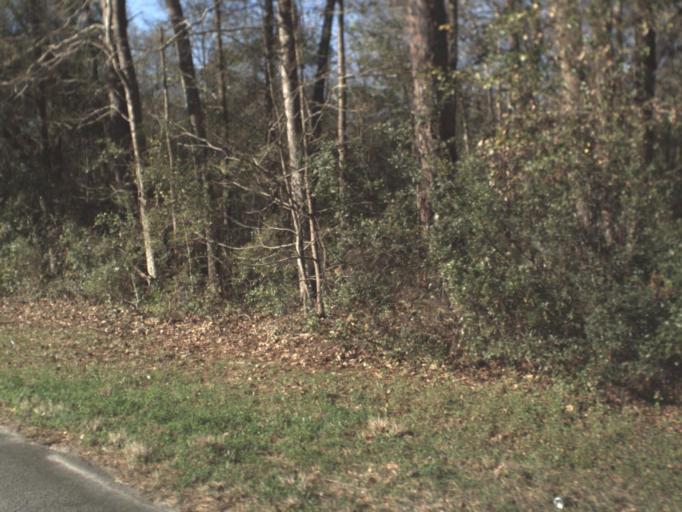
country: US
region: Georgia
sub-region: Brooks County
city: Quitman
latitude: 30.5786
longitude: -83.6370
